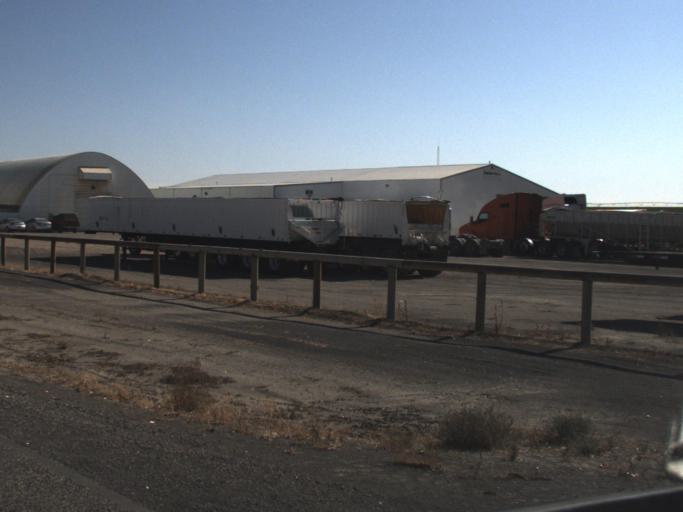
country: US
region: Washington
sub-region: Walla Walla County
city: Burbank
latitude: 46.2153
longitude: -118.9215
